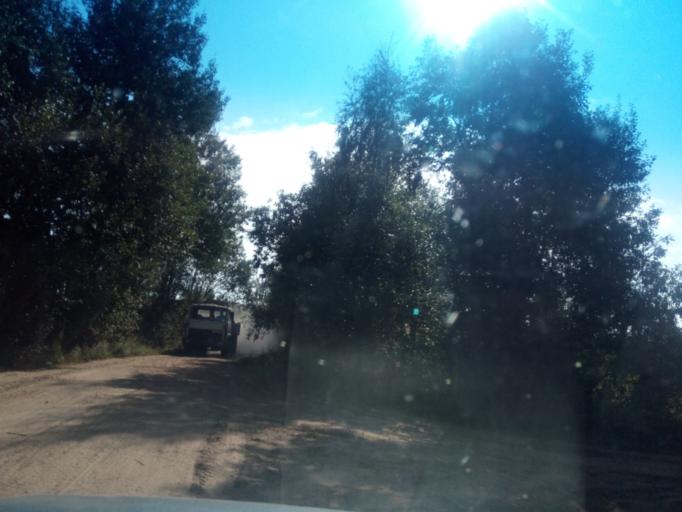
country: BY
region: Vitebsk
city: Dzisna
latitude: 55.6432
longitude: 28.2911
